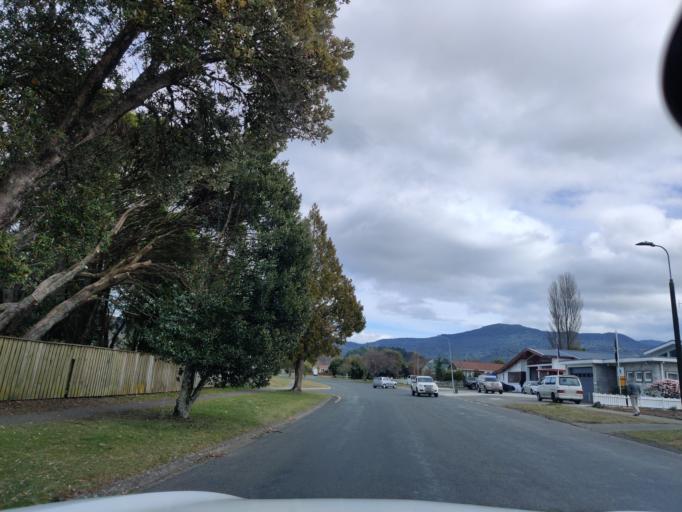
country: NZ
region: Waikato
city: Turangi
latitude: -38.9903
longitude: 175.8072
